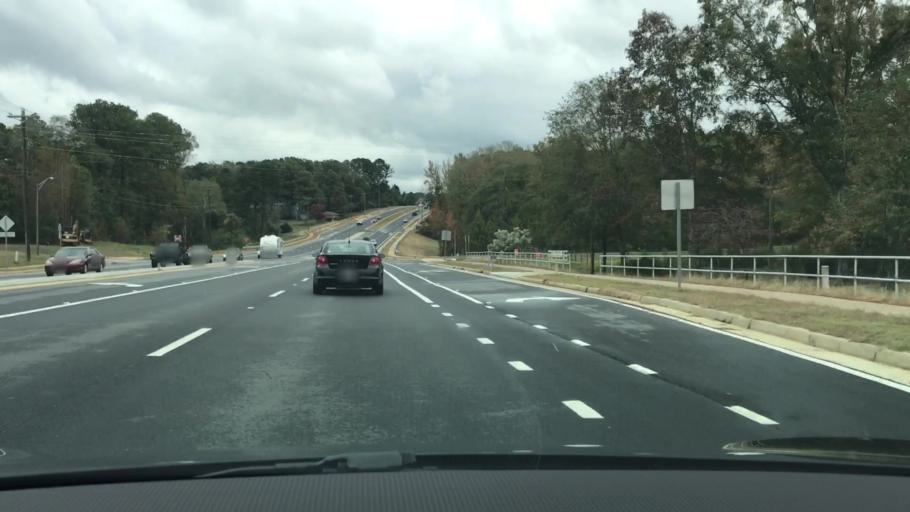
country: US
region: Georgia
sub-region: Oconee County
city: Watkinsville
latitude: 33.8915
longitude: -83.4585
